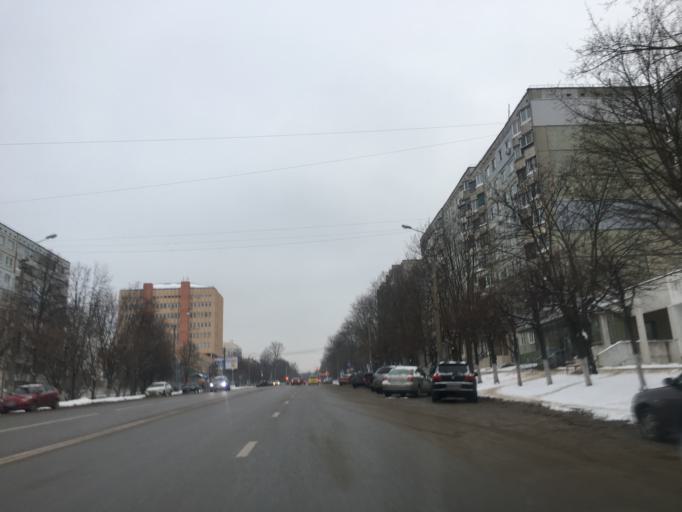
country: RU
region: Tula
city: Tula
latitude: 54.1940
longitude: 37.5910
